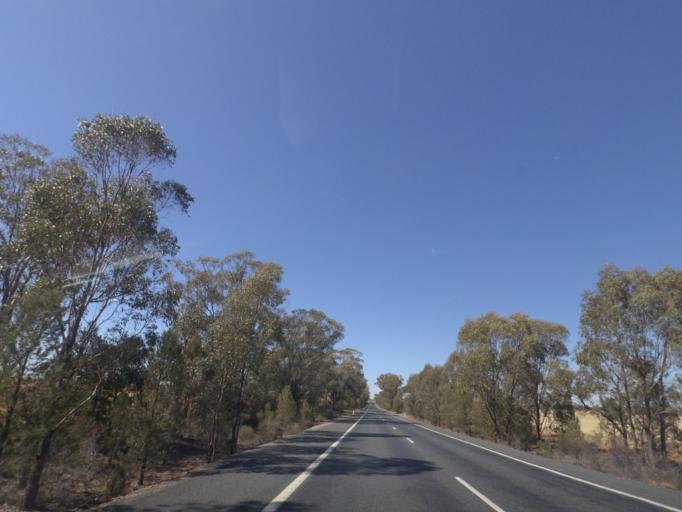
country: AU
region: New South Wales
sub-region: Bland
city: West Wyalong
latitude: -34.1718
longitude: 147.1149
